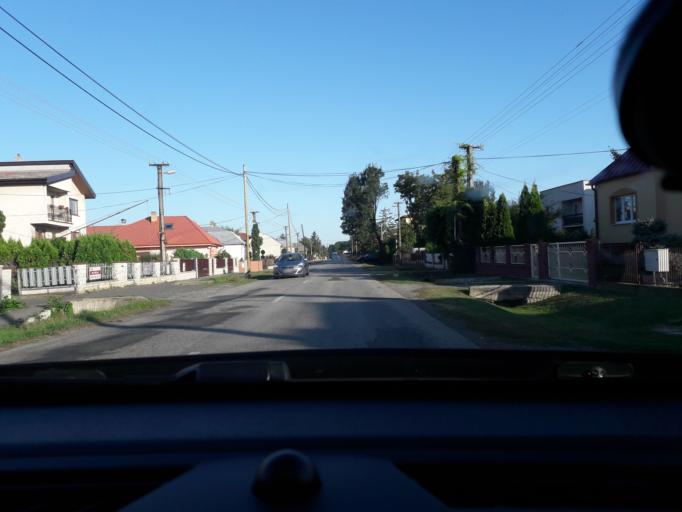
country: SK
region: Kosicky
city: Michalovce
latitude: 48.6342
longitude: 21.9266
